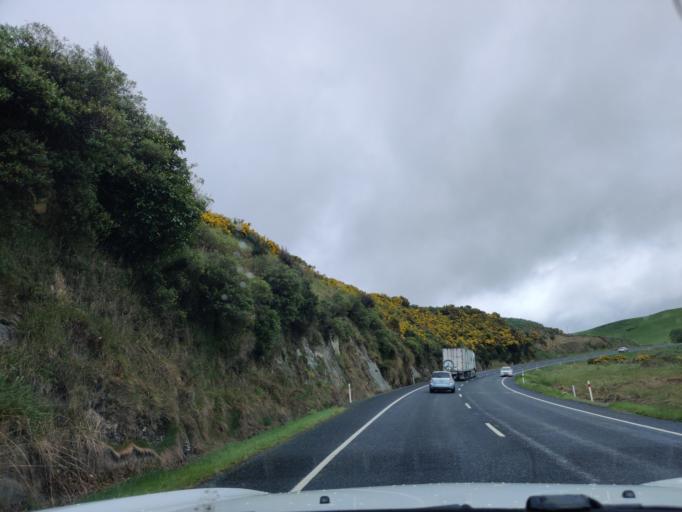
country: NZ
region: Manawatu-Wanganui
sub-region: Ruapehu District
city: Waiouru
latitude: -39.5514
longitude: 175.6873
